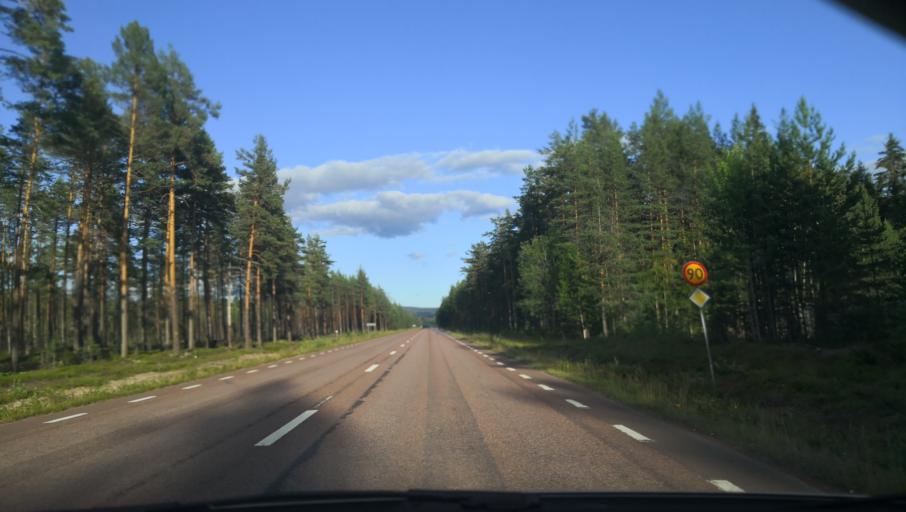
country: SE
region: Dalarna
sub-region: Alvdalens Kommun
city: AElvdalen
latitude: 61.2757
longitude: 13.9697
